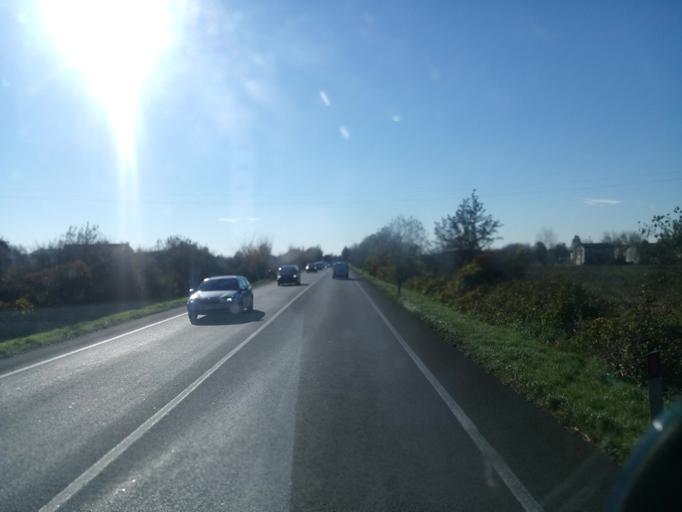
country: IT
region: Veneto
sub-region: Provincia di Padova
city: Borgoricco-San Michele delle Badesse-Sant'Eufemia
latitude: 45.5241
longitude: 11.9393
